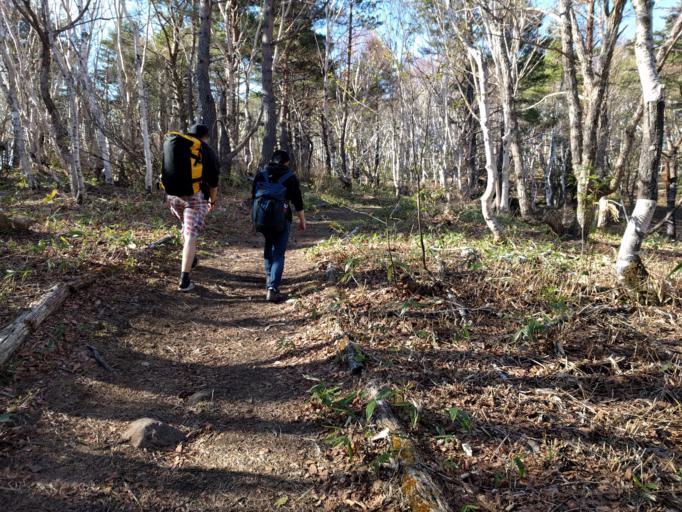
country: JP
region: Nagano
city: Nakano
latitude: 36.7218
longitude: 138.4775
